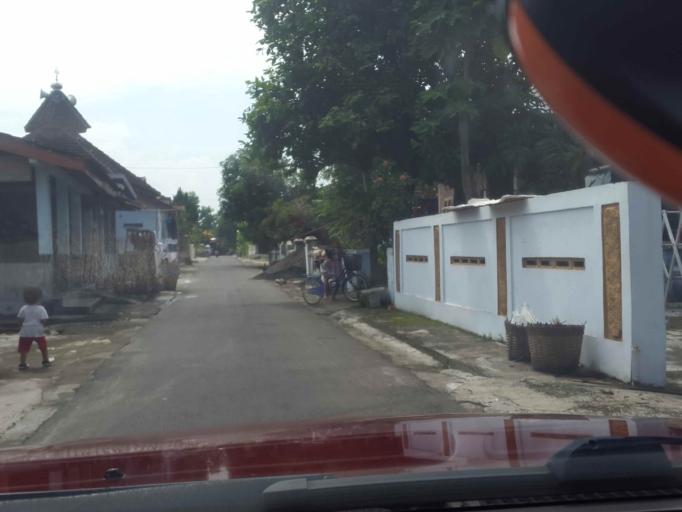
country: ID
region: Central Java
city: Jaten
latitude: -7.6009
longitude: 110.9435
